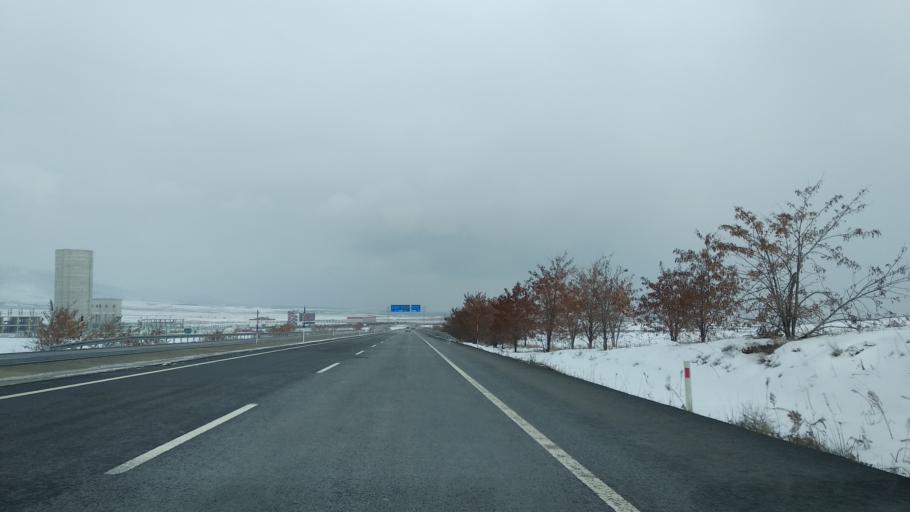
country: TR
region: Kayseri
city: Elbasi
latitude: 38.6339
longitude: 35.8478
